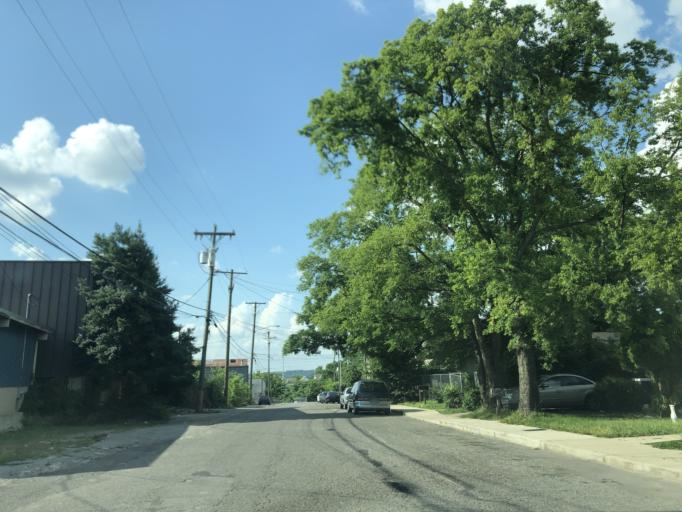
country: US
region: Tennessee
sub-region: Davidson County
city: Nashville
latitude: 36.1556
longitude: -86.8361
